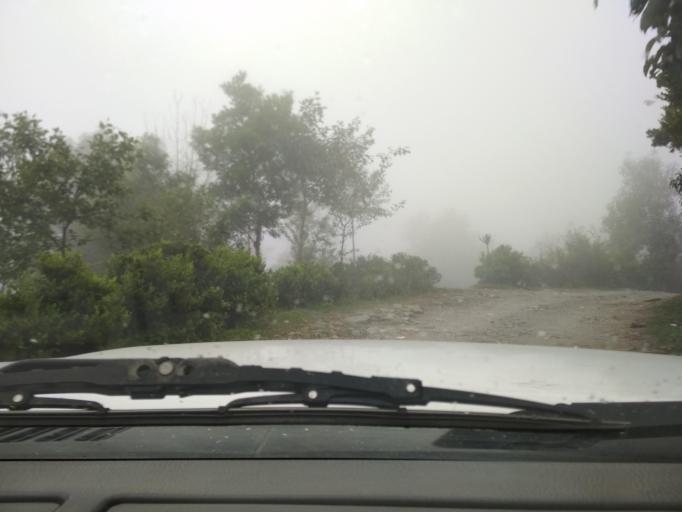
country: MX
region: Veracruz
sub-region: La Perla
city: Barrio de San Miguel
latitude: 18.9497
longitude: -97.1225
